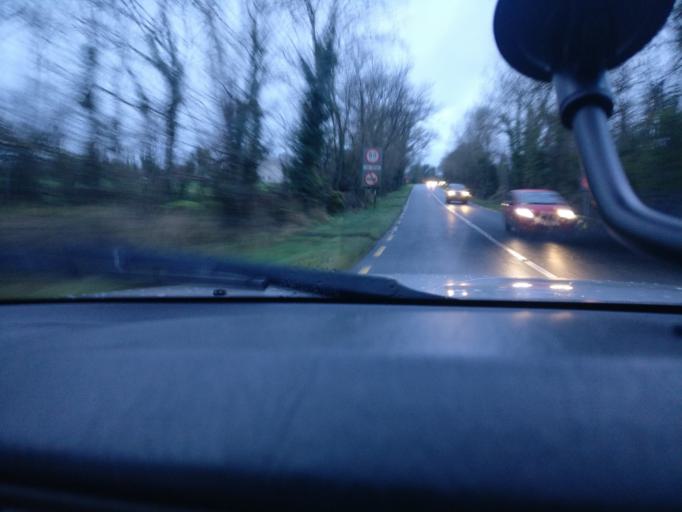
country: IE
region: Connaught
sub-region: County Galway
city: Ballinasloe
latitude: 53.2840
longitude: -8.3599
